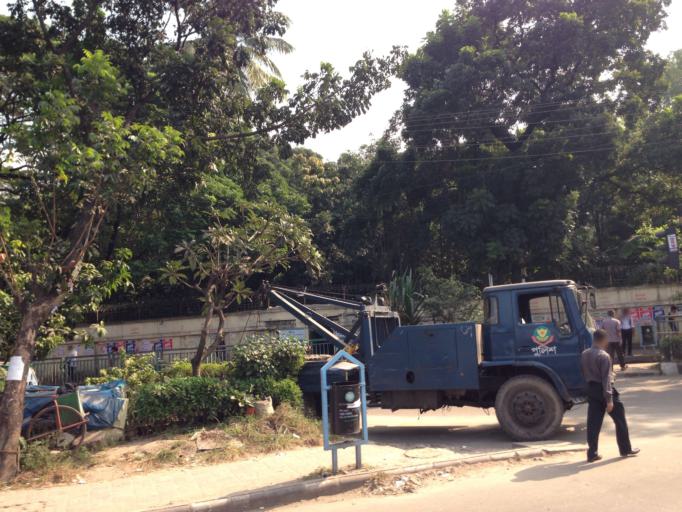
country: BD
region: Dhaka
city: Azimpur
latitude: 23.7406
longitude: 90.3833
